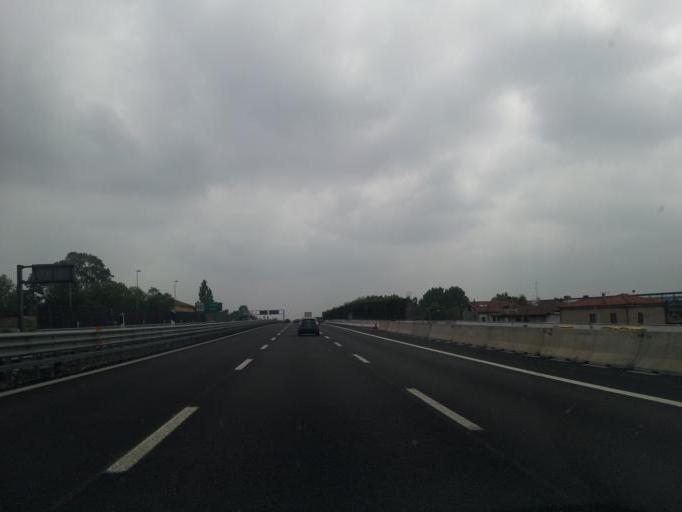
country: IT
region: Veneto
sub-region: Provincia di Padova
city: Vigodarzere
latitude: 45.4445
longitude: 11.8684
